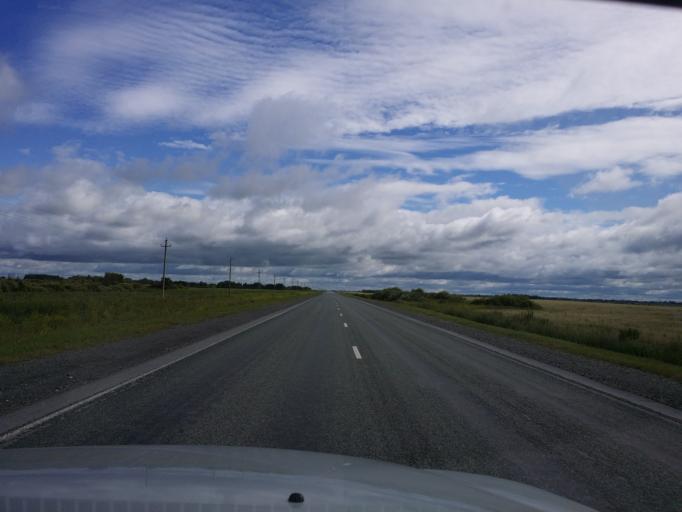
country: RU
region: Tjumen
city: Yarkovo
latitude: 57.2881
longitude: 66.8960
